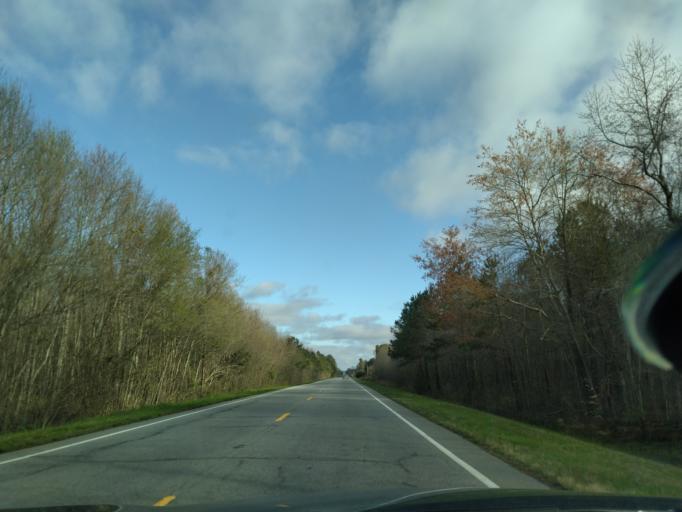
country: US
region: North Carolina
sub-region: Washington County
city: Plymouth
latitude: 35.9997
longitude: -76.7726
